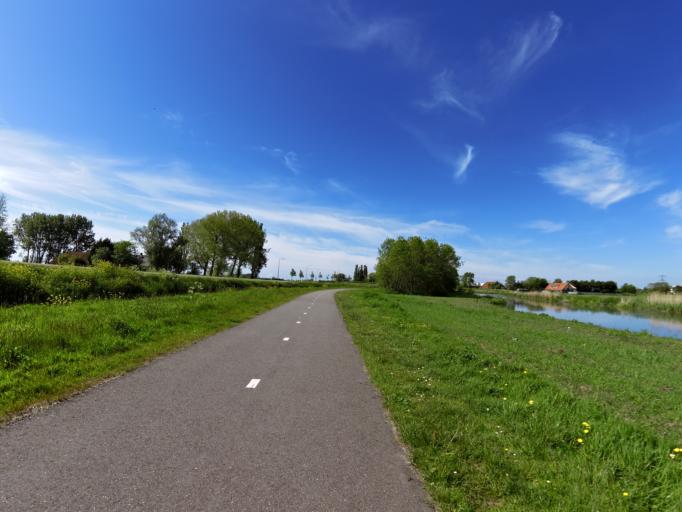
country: NL
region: South Holland
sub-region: Gemeente Hellevoetsluis
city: Nieuwenhoorn
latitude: 51.8737
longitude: 4.1553
